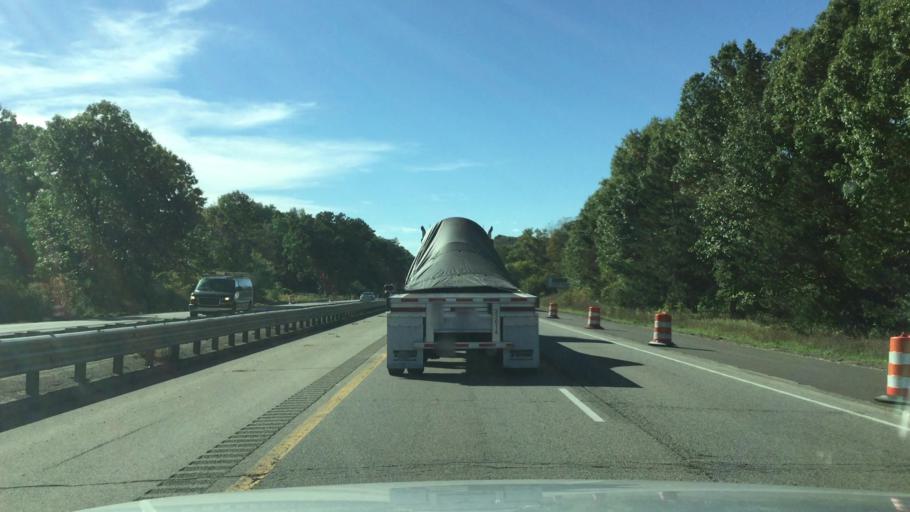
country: US
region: Michigan
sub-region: Jackson County
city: Michigan Center
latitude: 42.2774
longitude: -84.3393
